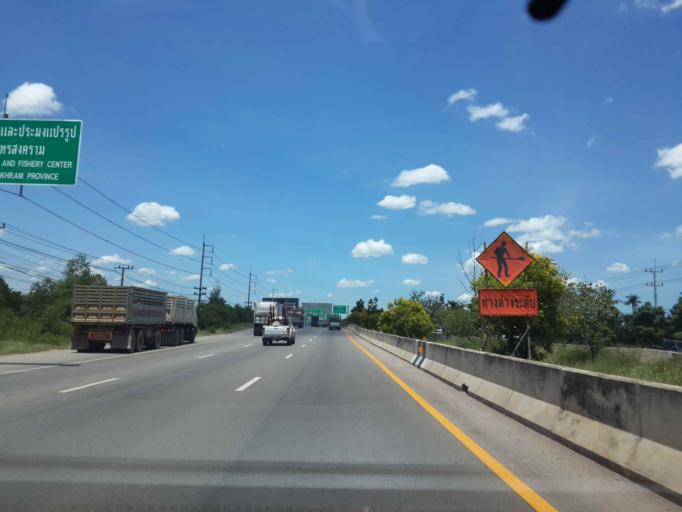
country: TH
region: Samut Songkhram
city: Amphawa
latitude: 13.3779
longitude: 99.9677
